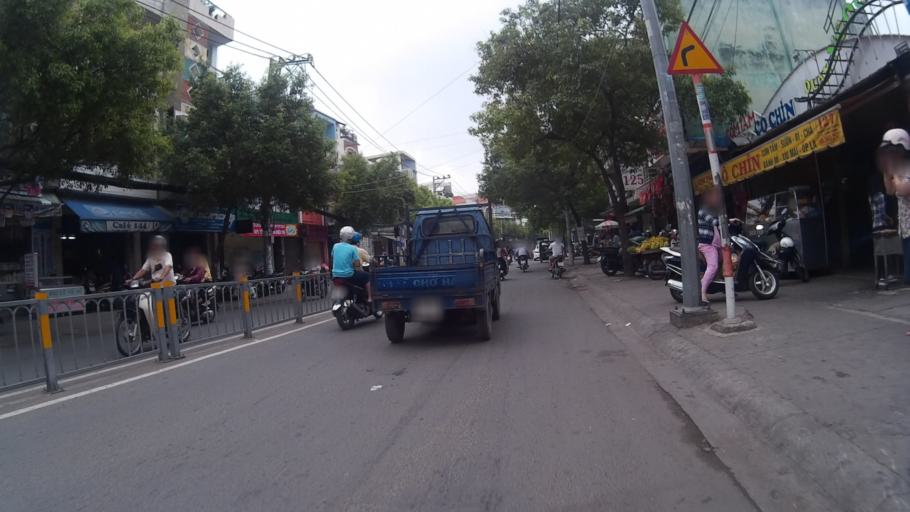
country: VN
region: Ho Chi Minh City
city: Quan Binh Thanh
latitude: 10.8082
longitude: 106.6882
